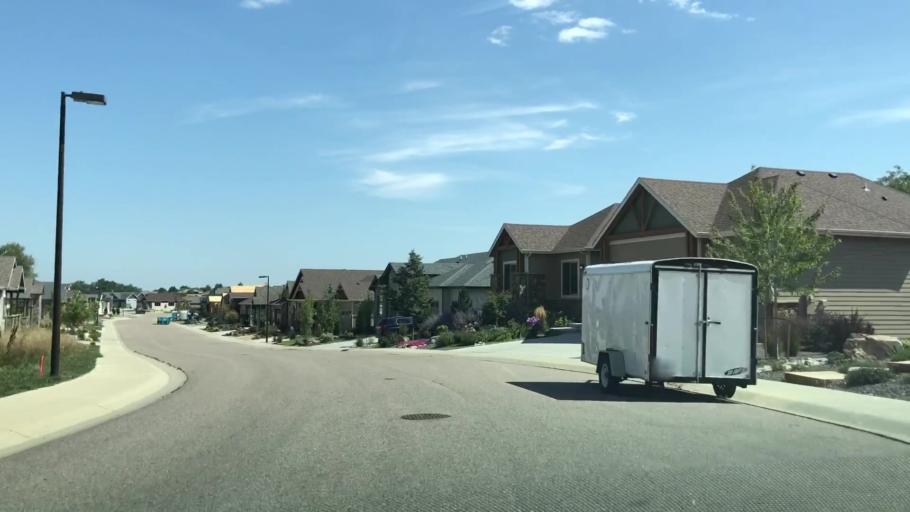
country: US
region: Colorado
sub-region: Larimer County
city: Loveland
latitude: 40.3973
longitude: -105.1573
